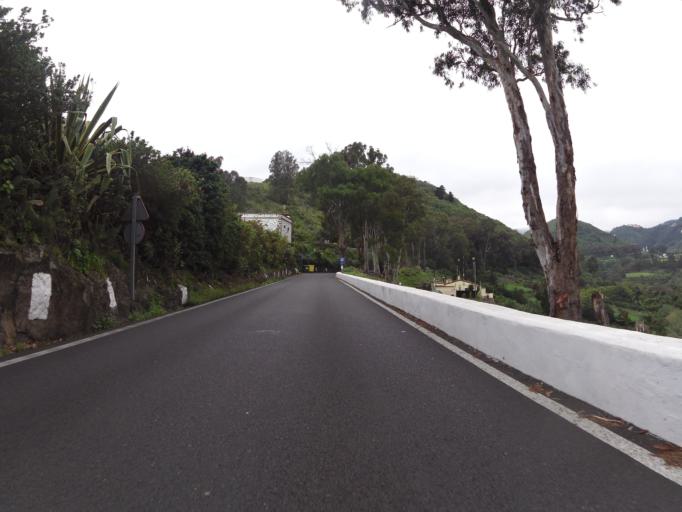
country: ES
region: Canary Islands
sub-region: Provincia de Las Palmas
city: Teror
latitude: 28.0784
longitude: -15.5188
